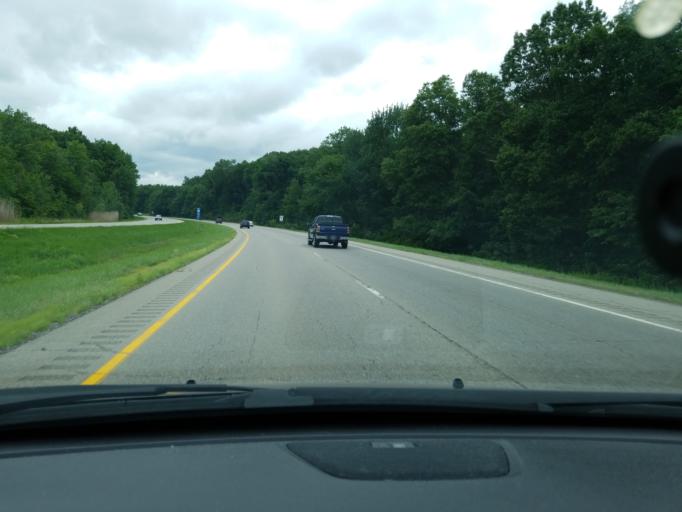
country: US
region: Ohio
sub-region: Lorain County
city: Amherst
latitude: 41.4107
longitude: -82.2485
